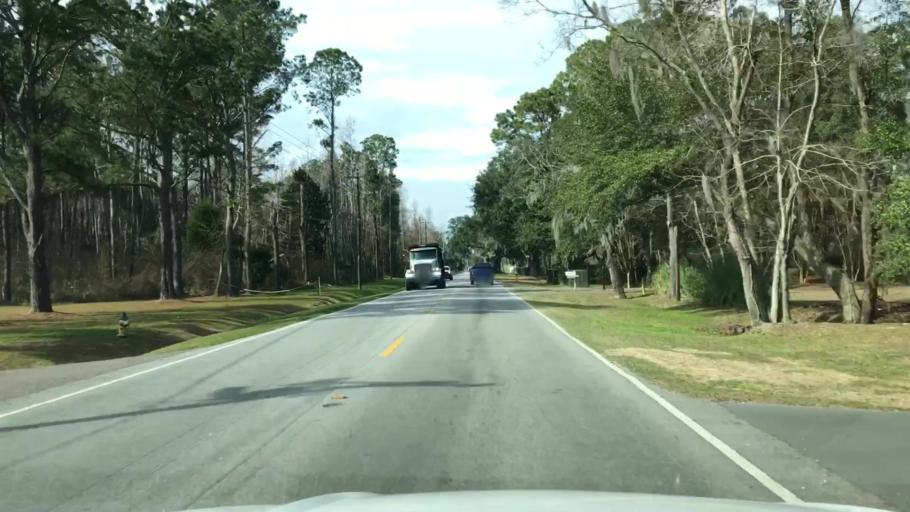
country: US
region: South Carolina
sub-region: Charleston County
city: Shell Point
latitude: 32.7702
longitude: -80.0768
